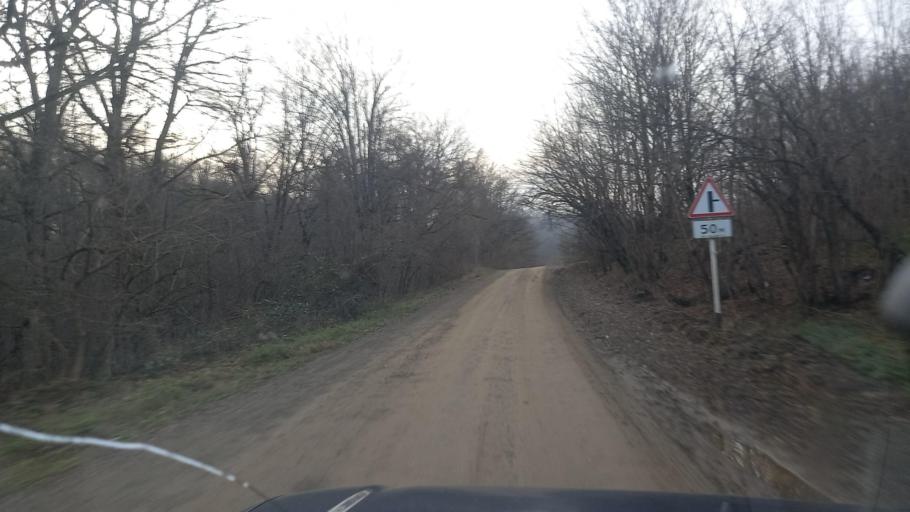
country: RU
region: Krasnodarskiy
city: Goryachiy Klyuch
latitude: 44.3783
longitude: 39.1972
